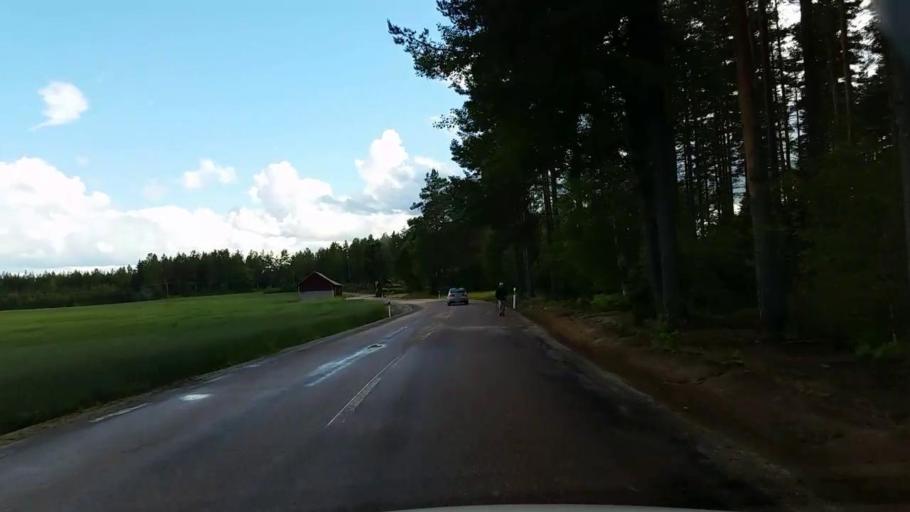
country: SE
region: Vaestmanland
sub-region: Fagersta Kommun
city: Fagersta
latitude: 59.9144
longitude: 15.8253
